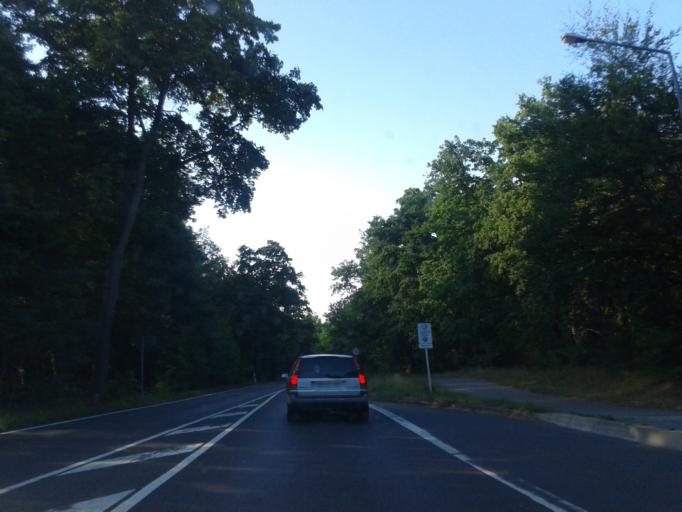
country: DE
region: Saxony
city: Radebeul
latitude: 51.1048
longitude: 13.7103
